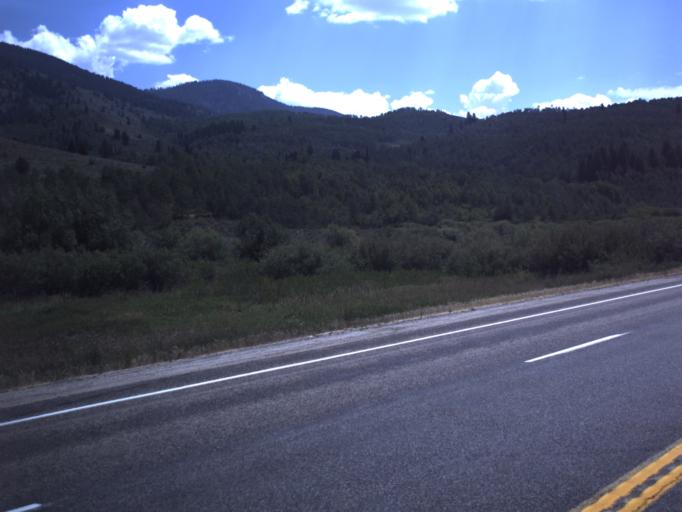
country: US
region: Utah
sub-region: Cache County
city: Richmond
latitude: 41.8731
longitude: -111.5663
